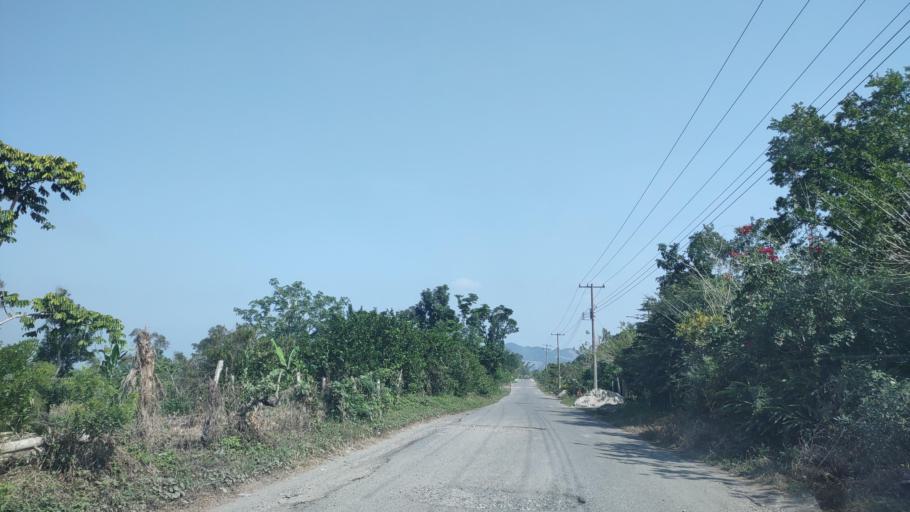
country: MX
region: Puebla
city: Espinal
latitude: 20.2591
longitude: -97.3187
